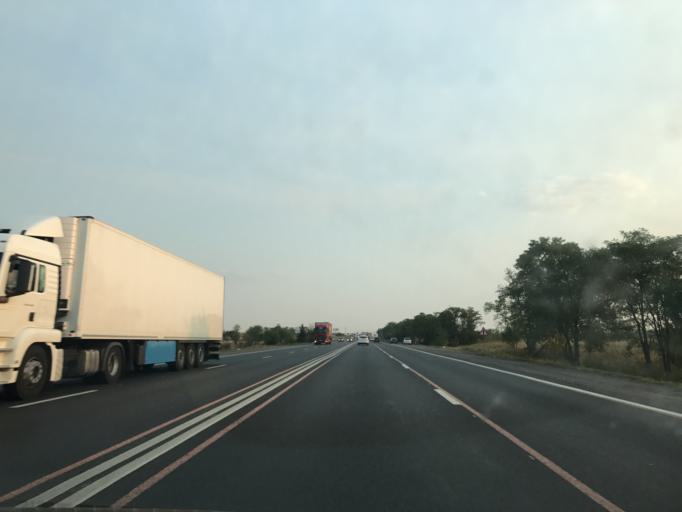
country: RU
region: Rostov
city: Kamensk-Shakhtinskiy
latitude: 48.2598
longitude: 40.2933
